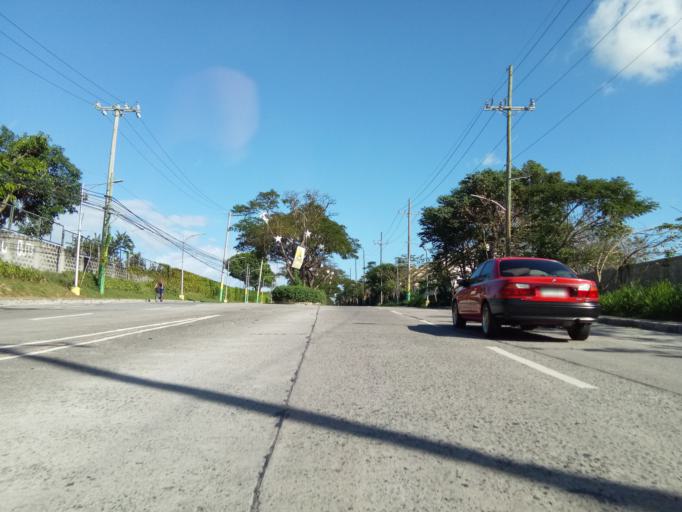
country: PH
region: Calabarzon
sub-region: Province of Cavite
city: Dasmarinas
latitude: 14.3512
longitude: 120.9572
